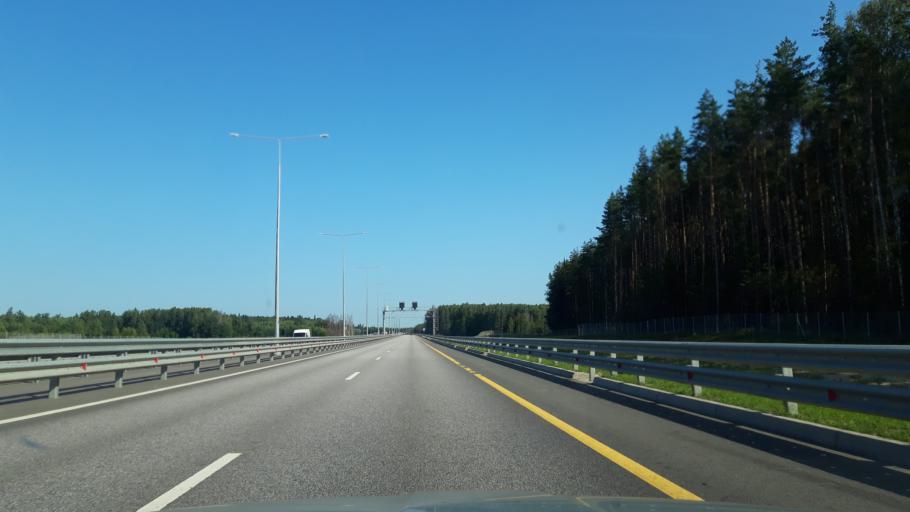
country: RU
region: Moskovskaya
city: Klin
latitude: 56.2715
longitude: 36.7244
